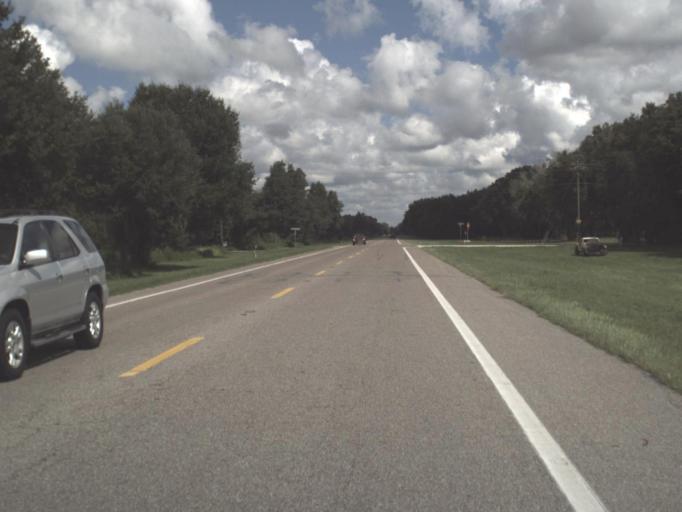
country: US
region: Florida
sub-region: Polk County
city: Polk City
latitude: 28.2211
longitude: -81.8205
